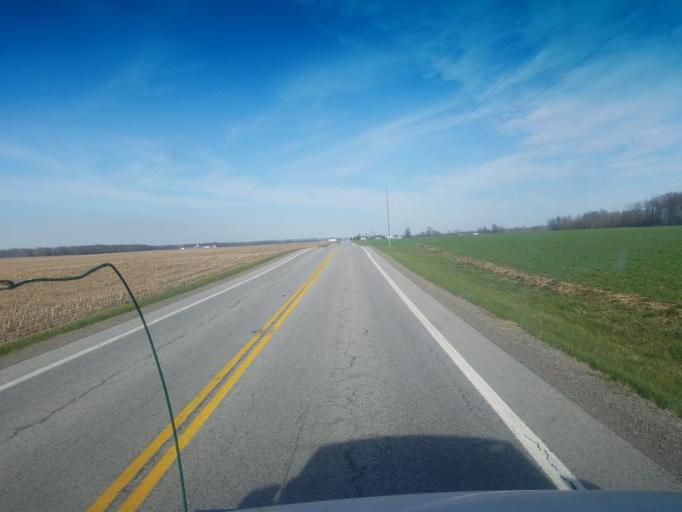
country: US
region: Ohio
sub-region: Logan County
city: De Graff
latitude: 40.3382
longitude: -83.9765
